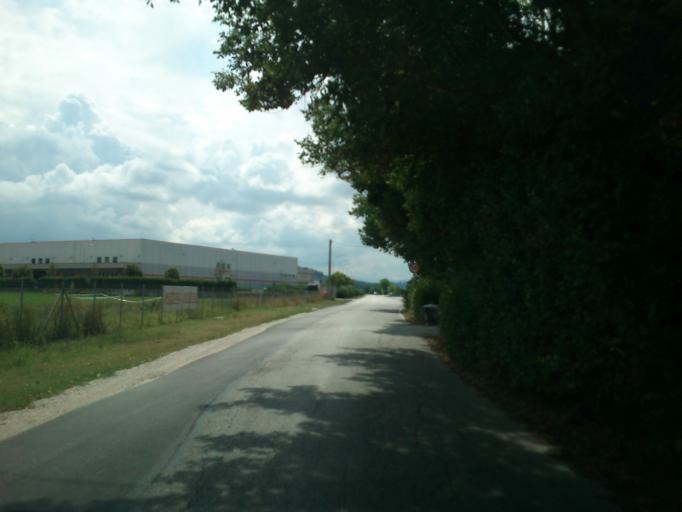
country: IT
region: The Marches
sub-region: Provincia di Pesaro e Urbino
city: Villanova
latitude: 43.7366
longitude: 12.9244
